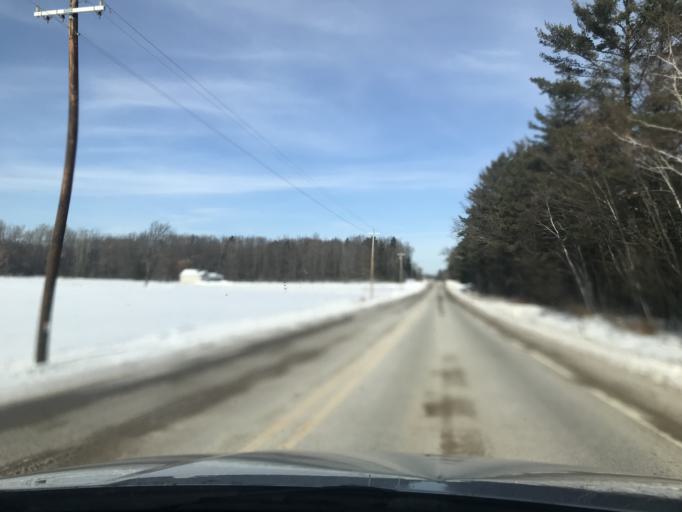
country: US
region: Wisconsin
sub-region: Oconto County
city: Oconto Falls
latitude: 45.1352
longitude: -88.1775
